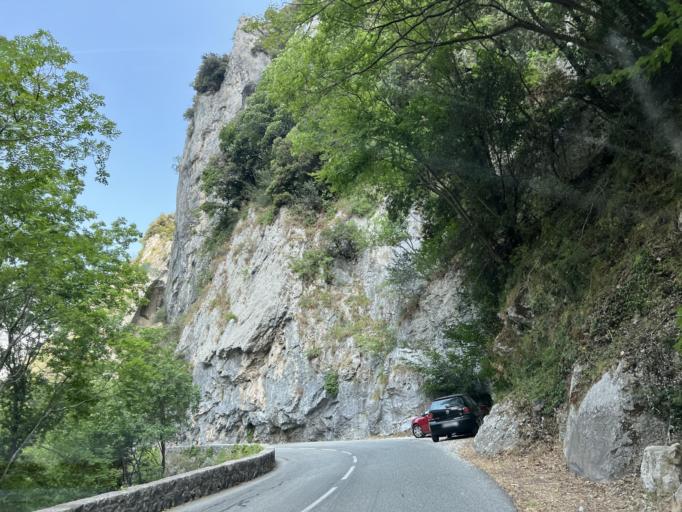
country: FR
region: Provence-Alpes-Cote d'Azur
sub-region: Departement des Alpes-Maritimes
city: Tourrettes-sur-Loup
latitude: 43.7405
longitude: 7.0007
